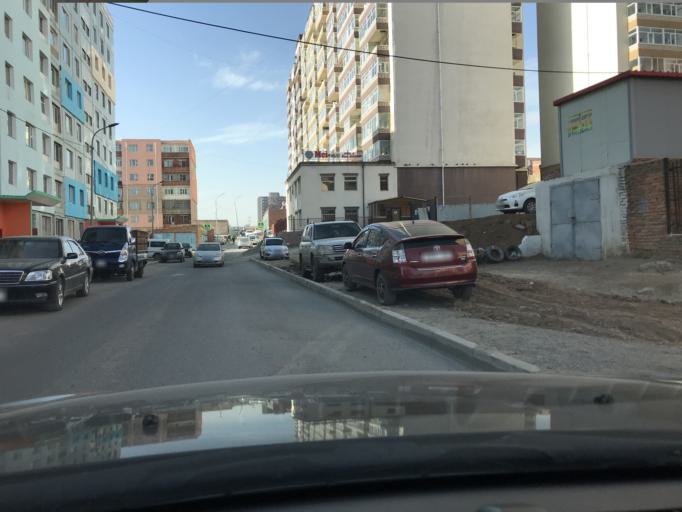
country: MN
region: Ulaanbaatar
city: Ulaanbaatar
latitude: 47.9203
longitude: 106.9577
